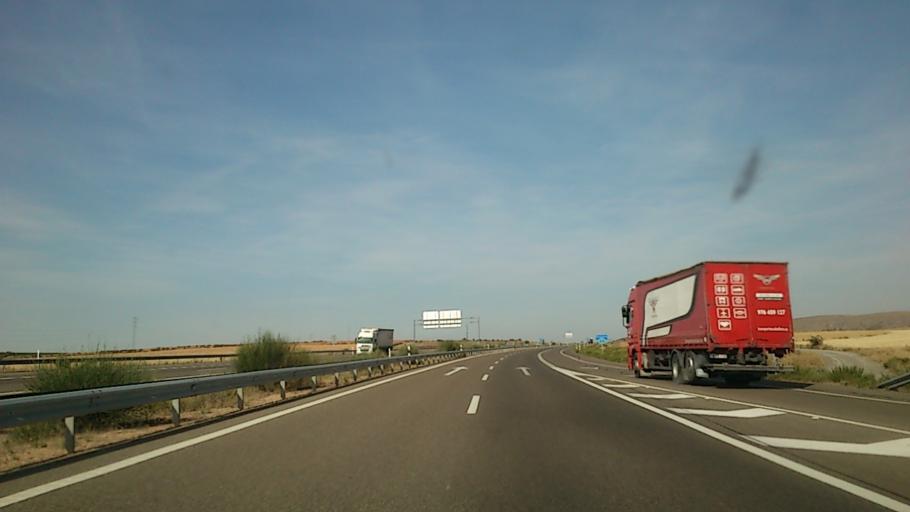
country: ES
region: Aragon
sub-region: Provincia de Zaragoza
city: Longares
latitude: 41.4103
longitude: -1.1720
